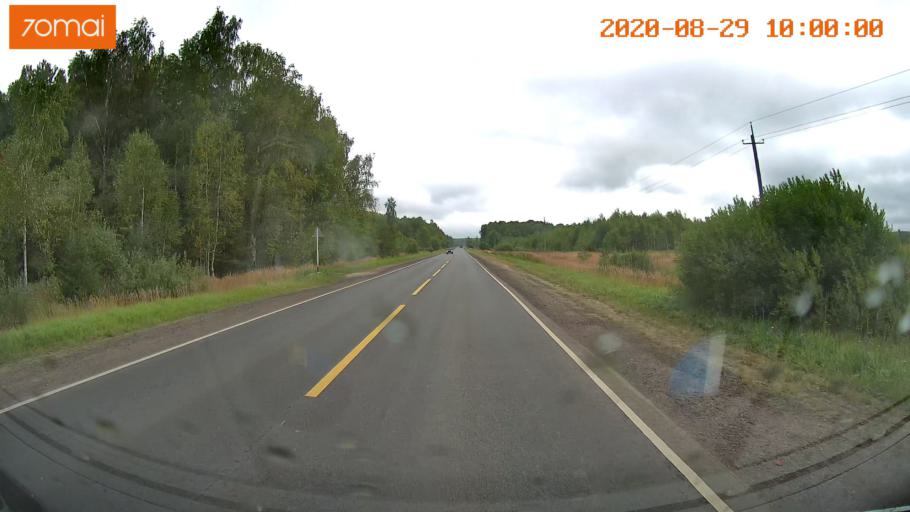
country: RU
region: Ivanovo
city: Zarechnyy
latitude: 57.4103
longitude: 42.3812
